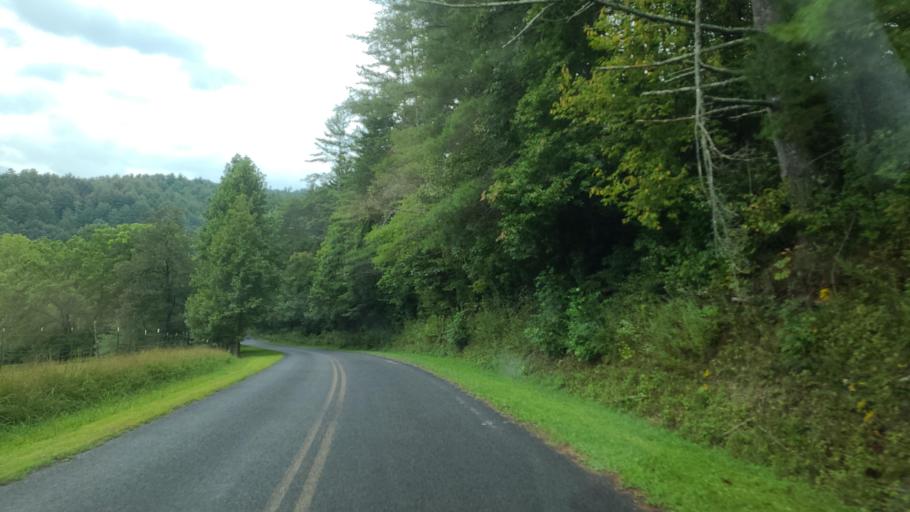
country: US
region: Georgia
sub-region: Gilmer County
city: Ellijay
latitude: 34.7995
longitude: -84.5615
